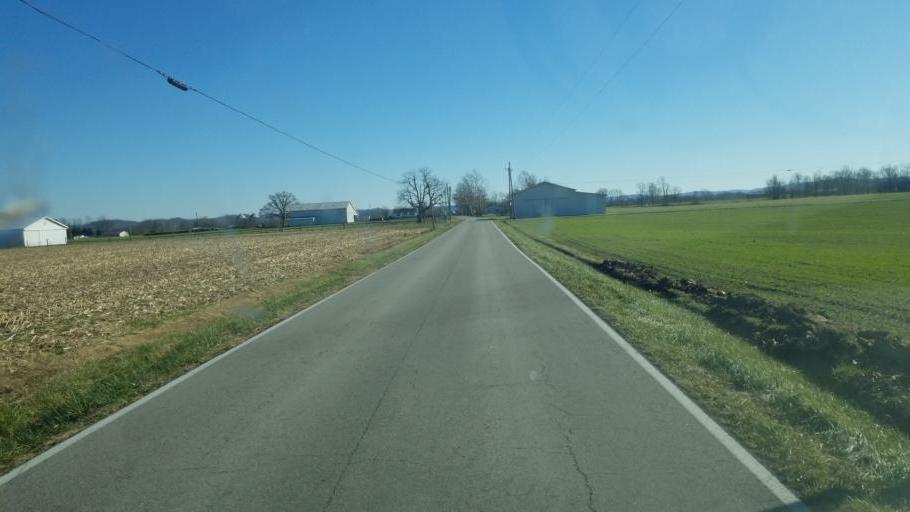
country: US
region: Ohio
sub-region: Adams County
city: Manchester
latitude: 38.5372
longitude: -83.6307
